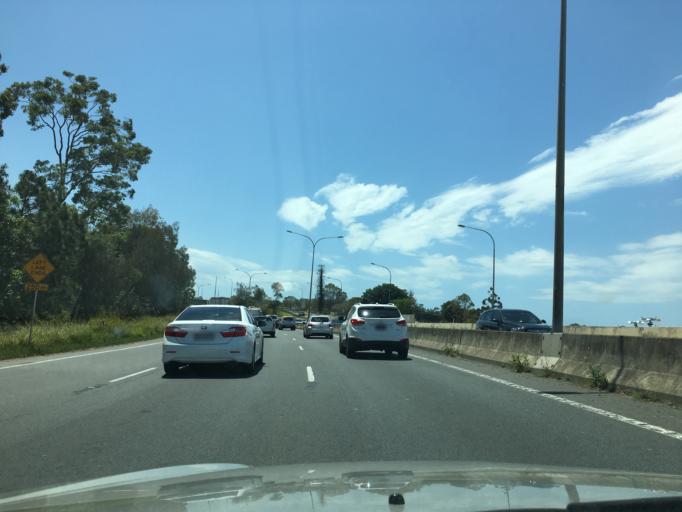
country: AU
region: Queensland
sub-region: Brisbane
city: Shorncliffe
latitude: -27.3760
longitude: 153.0962
